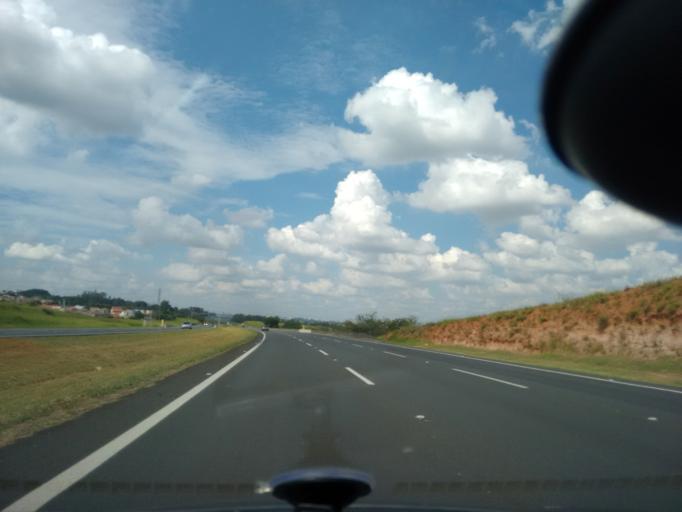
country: BR
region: Sao Paulo
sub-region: Hortolandia
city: Hortolandia
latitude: -22.9128
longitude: -47.1854
